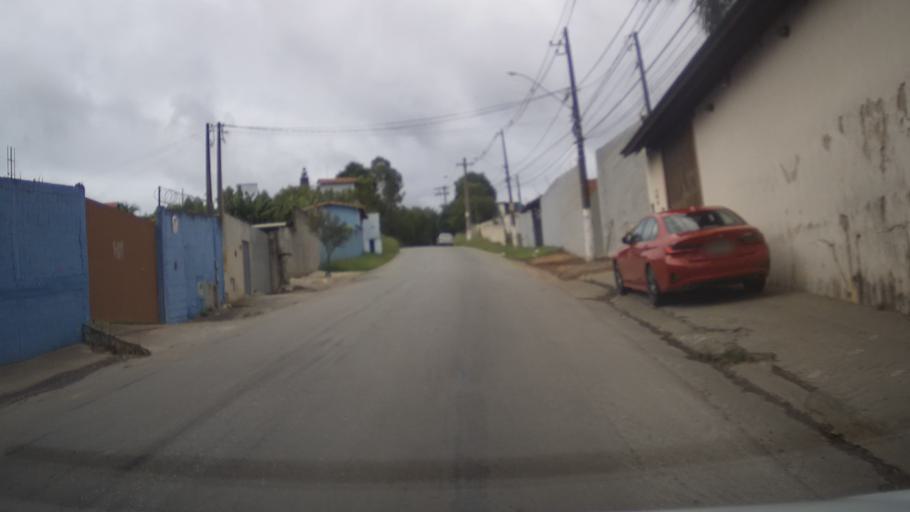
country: BR
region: Sao Paulo
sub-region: Aruja
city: Aruja
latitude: -23.3827
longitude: -46.3074
